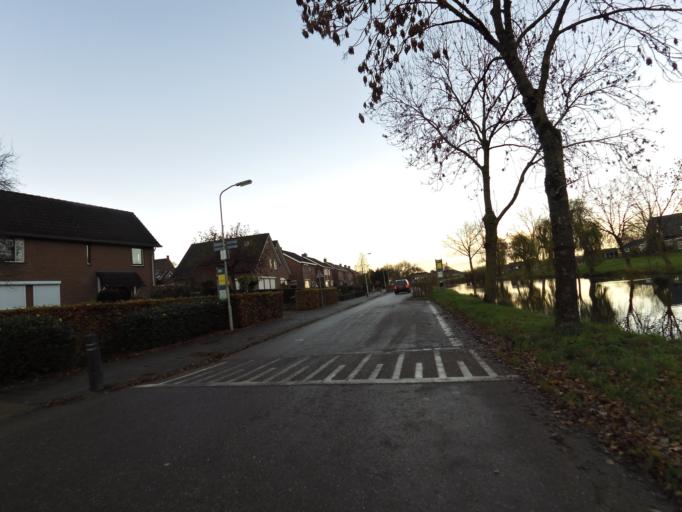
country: NL
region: Gelderland
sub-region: Gemeente Montferland
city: s-Heerenberg
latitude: 51.8850
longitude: 6.3062
